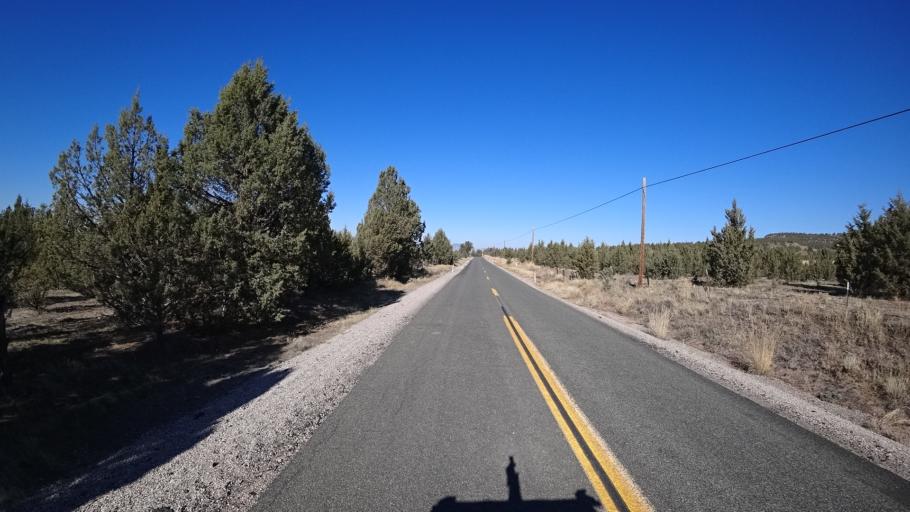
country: US
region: California
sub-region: Siskiyou County
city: Montague
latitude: 41.6361
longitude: -122.3393
